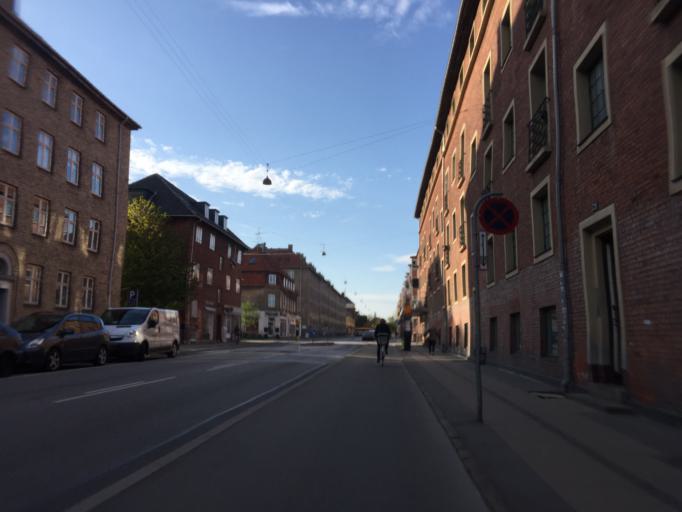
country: DK
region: Capital Region
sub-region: Kobenhavn
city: Vanlose
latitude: 55.6899
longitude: 12.4885
